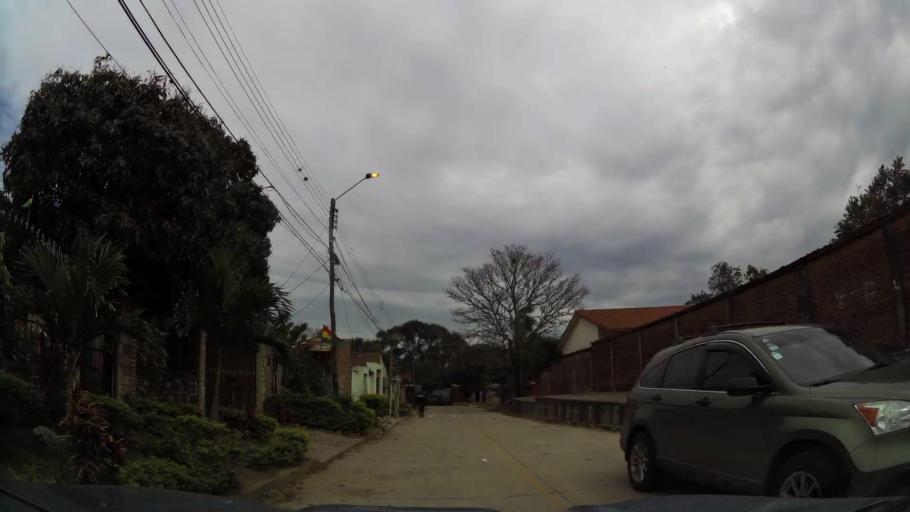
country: BO
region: Santa Cruz
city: Santa Cruz de la Sierra
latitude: -17.7444
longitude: -63.1938
